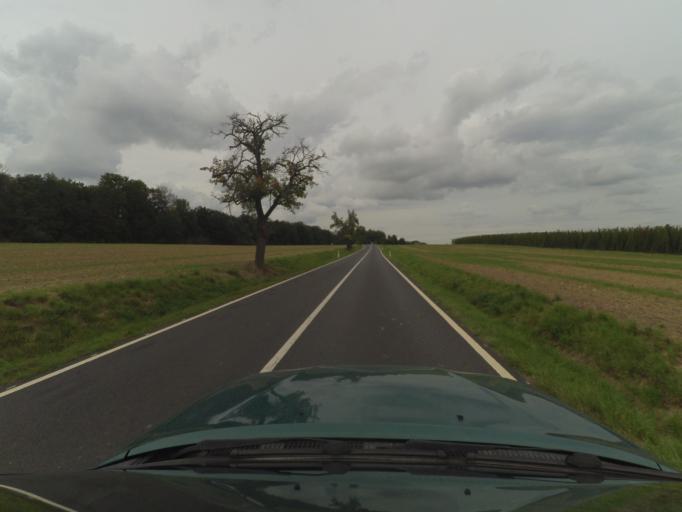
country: CZ
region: Ustecky
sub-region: Okres Louny
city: Louny
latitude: 50.2707
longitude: 13.7716
